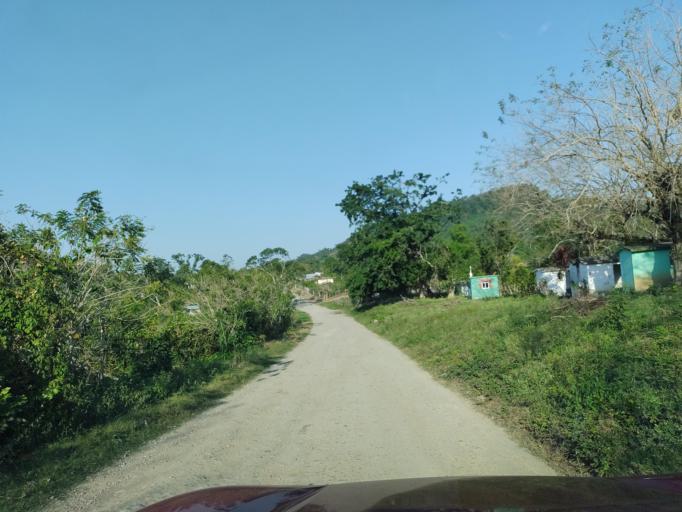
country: MX
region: Veracruz
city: Agua Dulce
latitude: 20.2818
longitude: -97.2509
